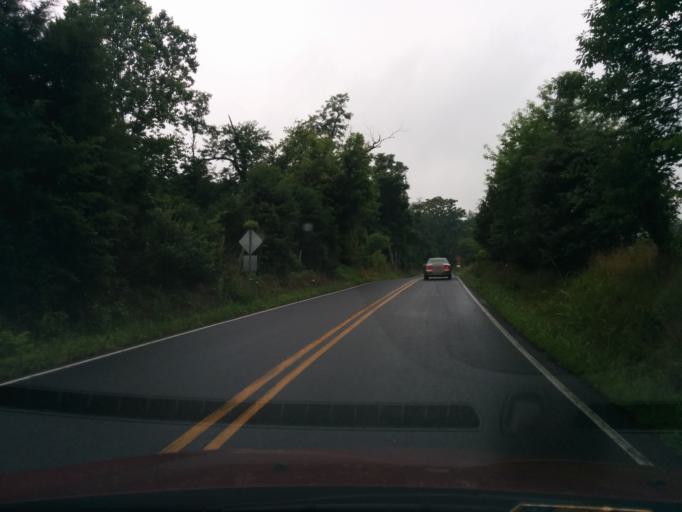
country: US
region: Virginia
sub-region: Rockbridge County
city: East Lexington
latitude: 37.8476
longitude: -79.3984
